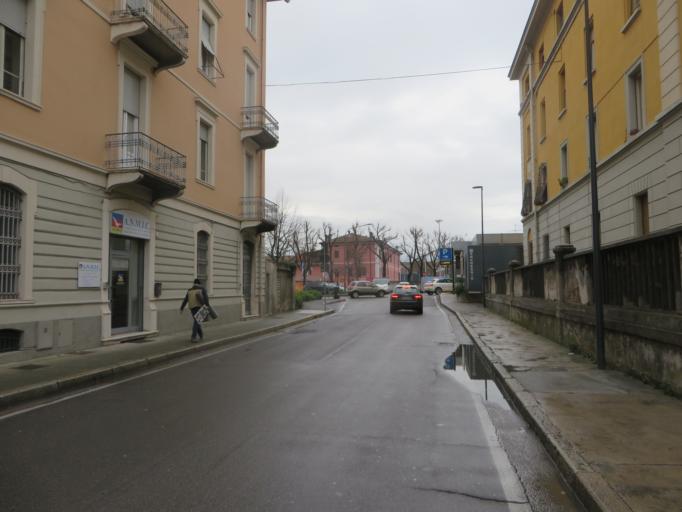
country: IT
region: Lombardy
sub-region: Provincia di Brescia
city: Brescia
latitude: 45.5313
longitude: 10.2231
